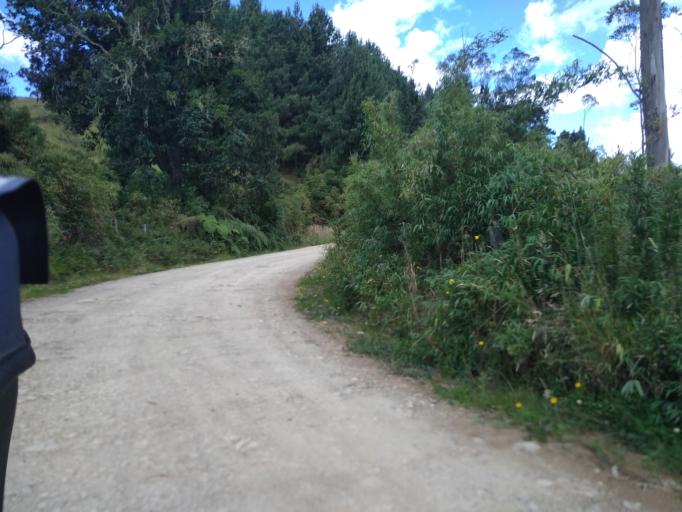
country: CO
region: Boyaca
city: Duitama
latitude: 5.9414
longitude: -73.1261
